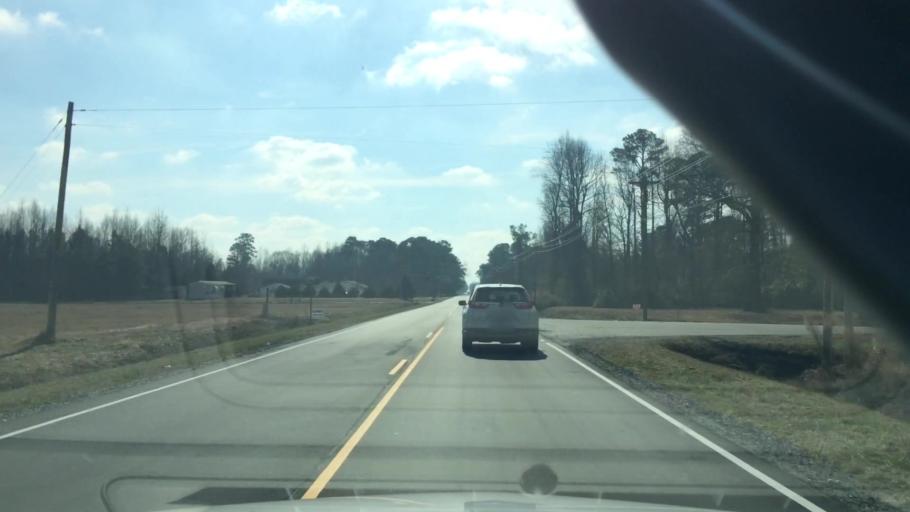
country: US
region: North Carolina
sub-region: Duplin County
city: Beulaville
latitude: 34.9675
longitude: -77.7630
